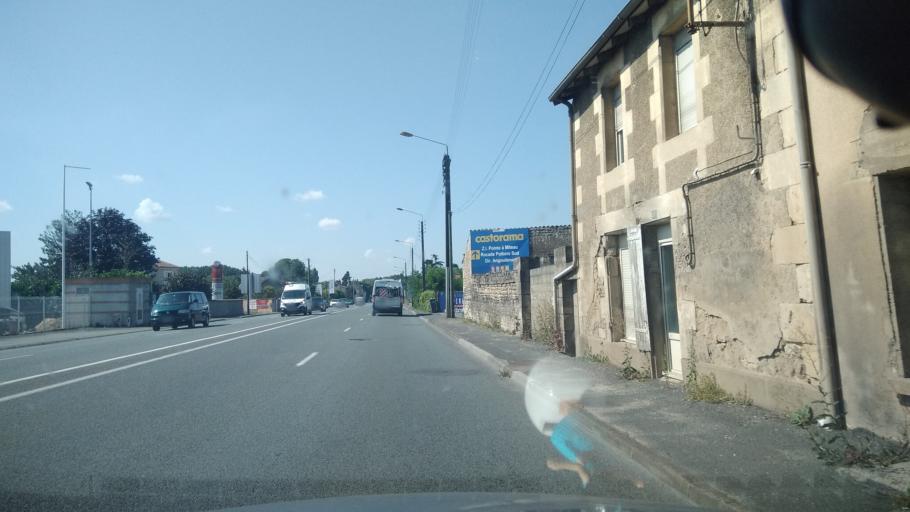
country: FR
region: Poitou-Charentes
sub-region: Departement de la Vienne
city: Chasseneuil-du-Poitou
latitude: 46.6428
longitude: 0.3606
